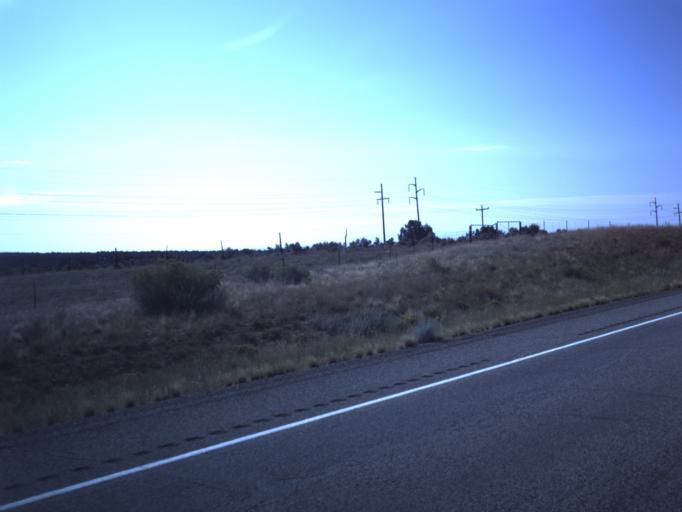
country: US
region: Utah
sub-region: San Juan County
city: Blanding
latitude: 37.5453
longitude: -109.4920
